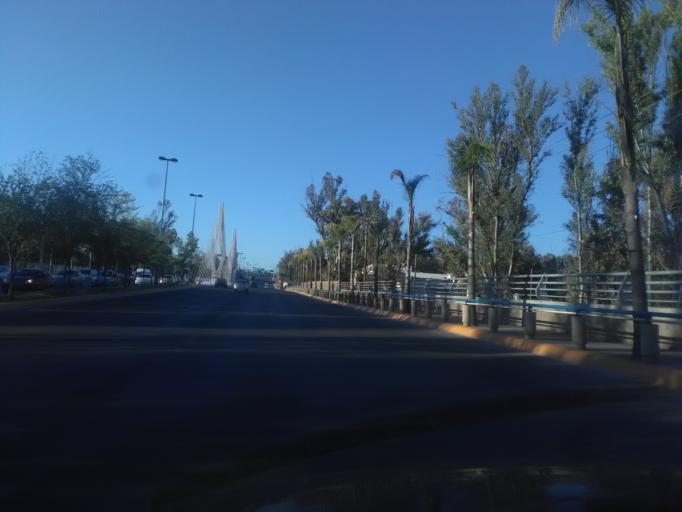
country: MX
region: Durango
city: Victoria de Durango
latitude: 24.0254
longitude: -104.6907
